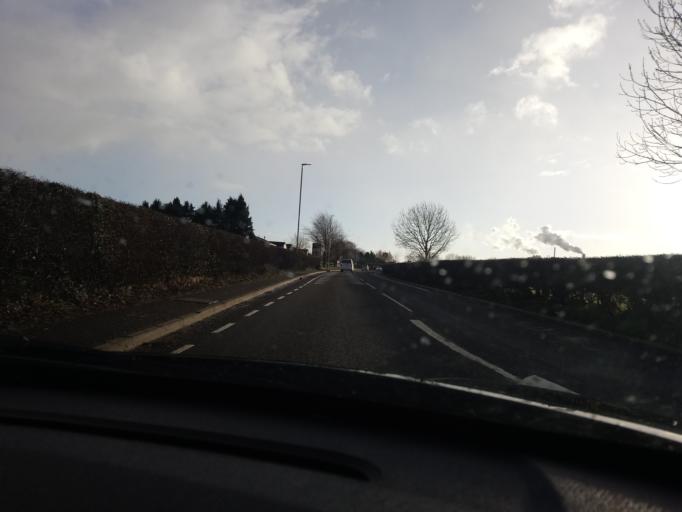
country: GB
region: Wales
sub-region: Wrexham
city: Chirk
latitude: 52.9461
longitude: -3.0592
